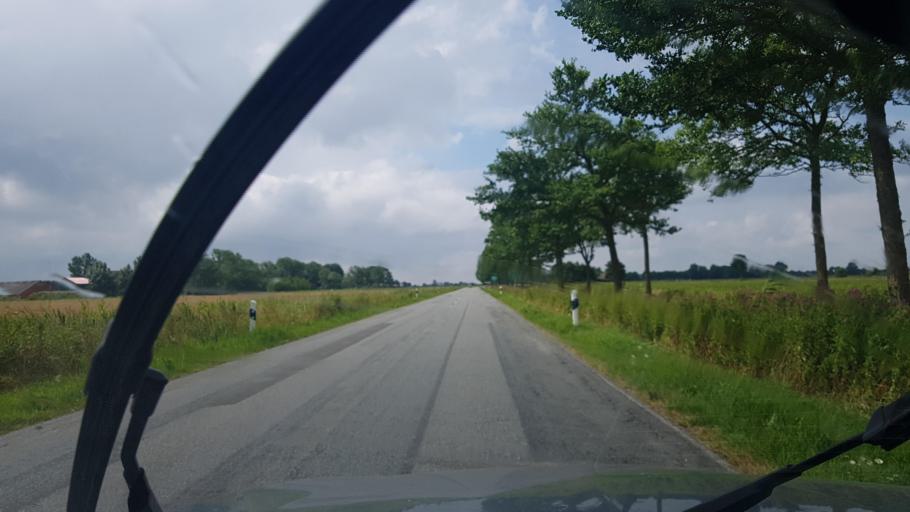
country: DE
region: Schleswig-Holstein
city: Elisabeth-Sophien-Koog
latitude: 54.4909
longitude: 8.9047
